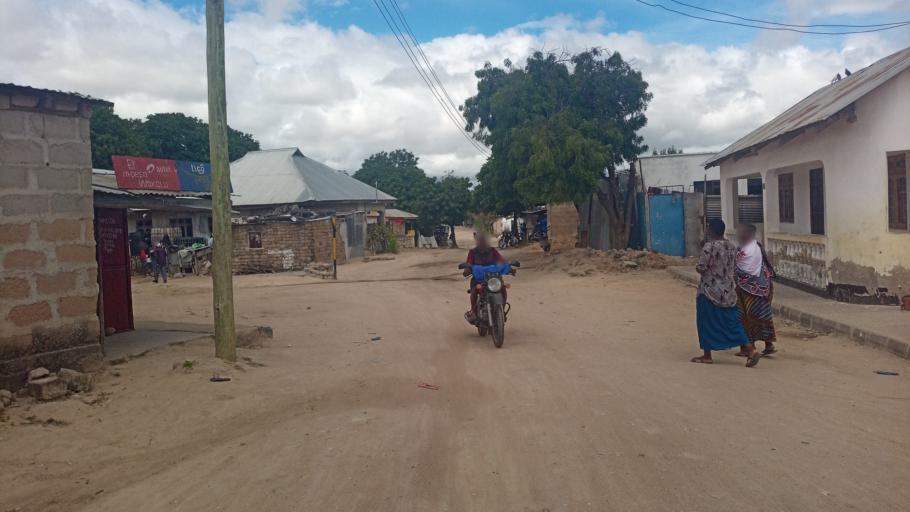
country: TZ
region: Dodoma
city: Dodoma
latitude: -6.1864
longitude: 35.7283
